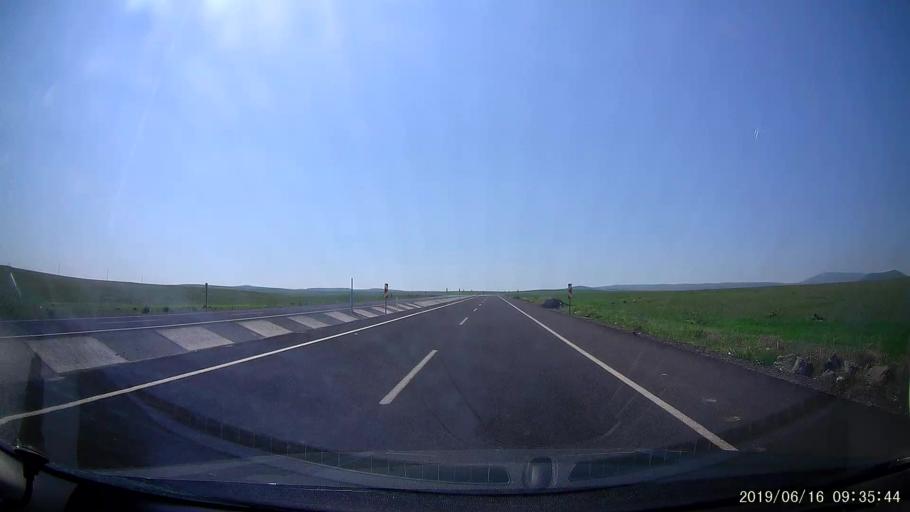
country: TR
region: Kars
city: Kars
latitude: 40.5673
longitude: 43.1609
